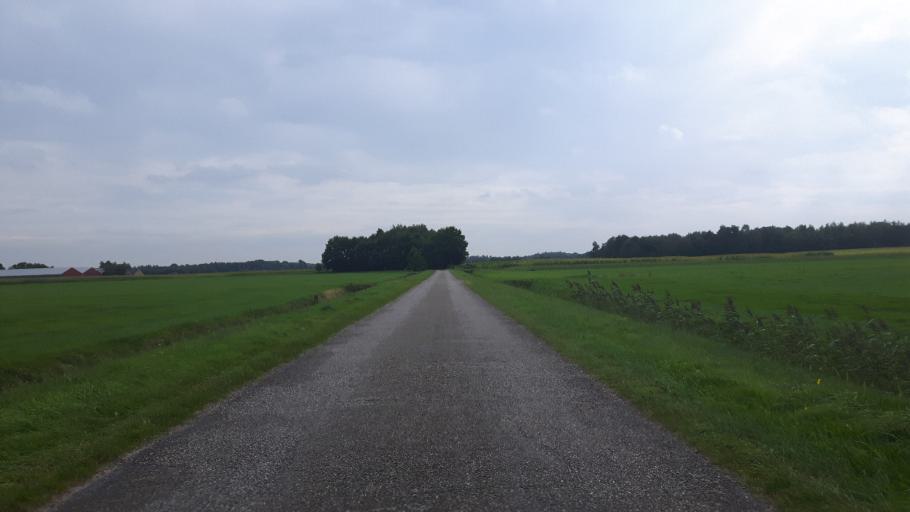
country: NL
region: Friesland
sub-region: Gemeente Weststellingwerf
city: Noordwolde
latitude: 52.9557
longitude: 6.2702
